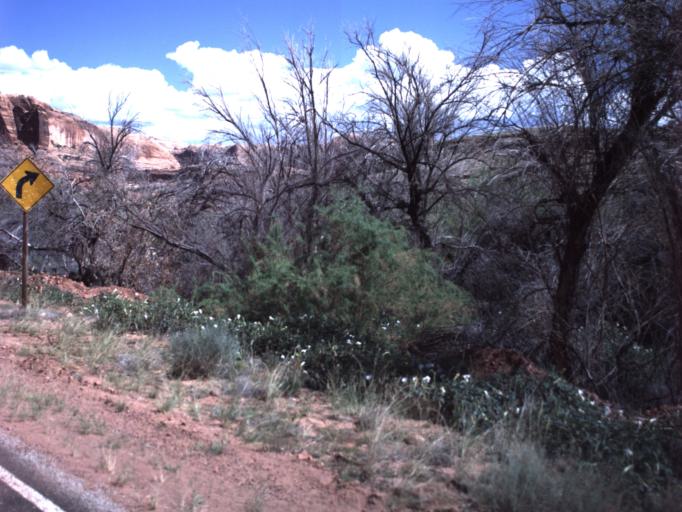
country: US
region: Utah
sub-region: Grand County
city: Moab
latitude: 38.5787
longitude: -109.6455
